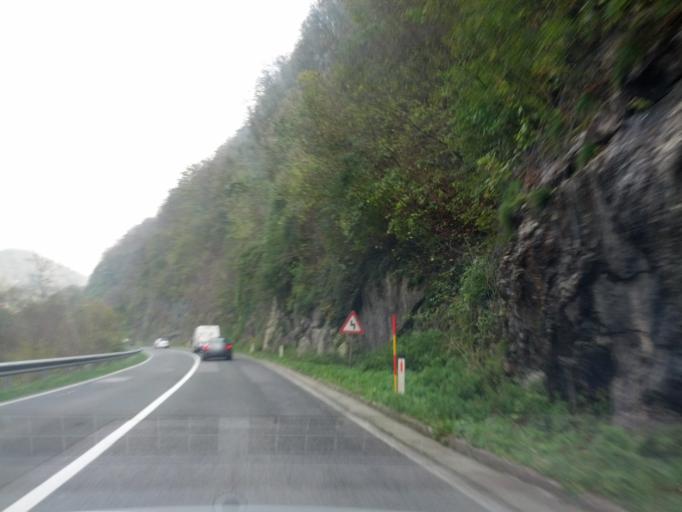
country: SI
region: Zagorje ob Savi
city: Zagorje ob Savi
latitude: 46.1128
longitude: 14.9819
